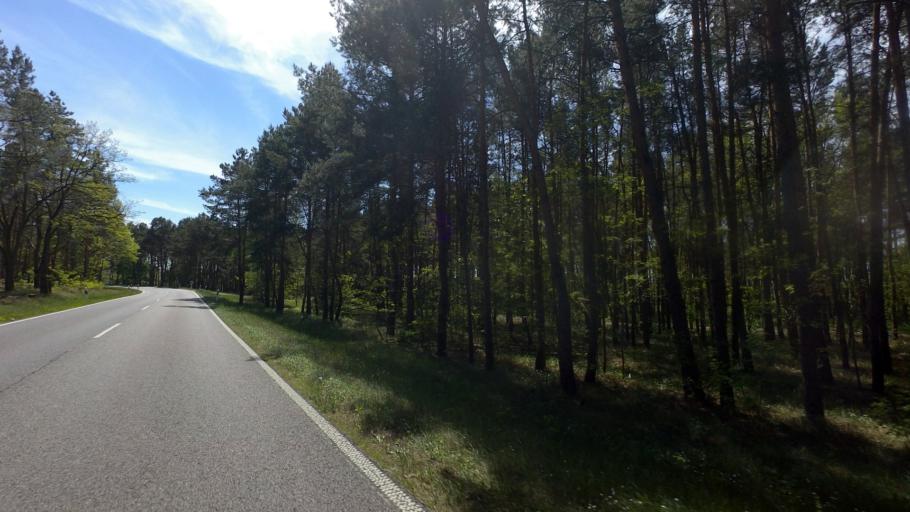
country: DE
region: Brandenburg
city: Luckenwalde
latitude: 52.1449
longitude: 13.1152
